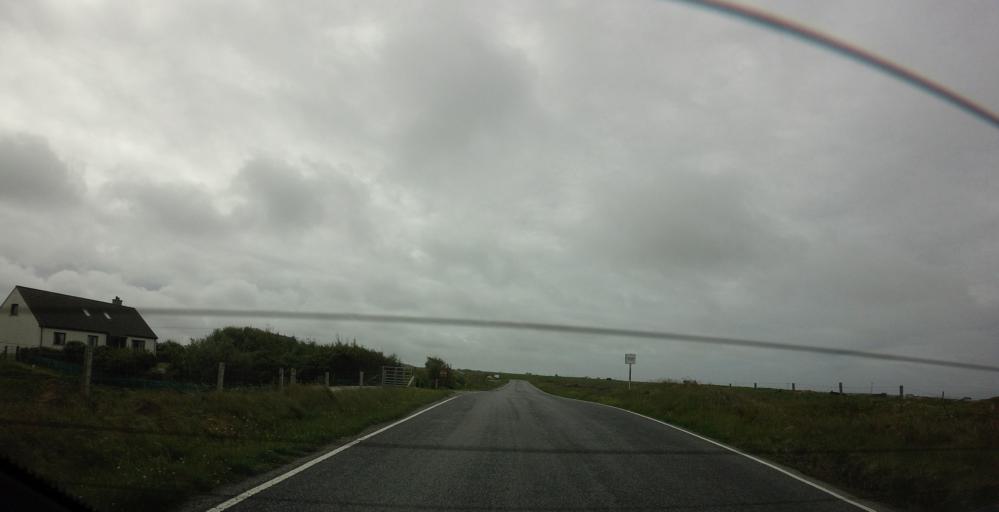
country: GB
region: Scotland
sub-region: Eilean Siar
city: Isle of South Uist
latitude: 57.2098
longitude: -7.3939
